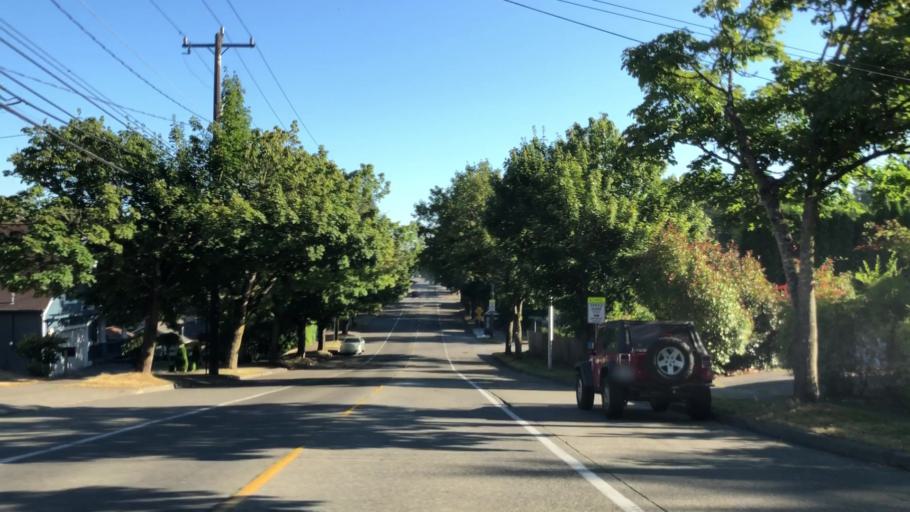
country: US
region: Washington
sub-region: King County
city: White Center
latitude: 47.5375
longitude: -122.3551
